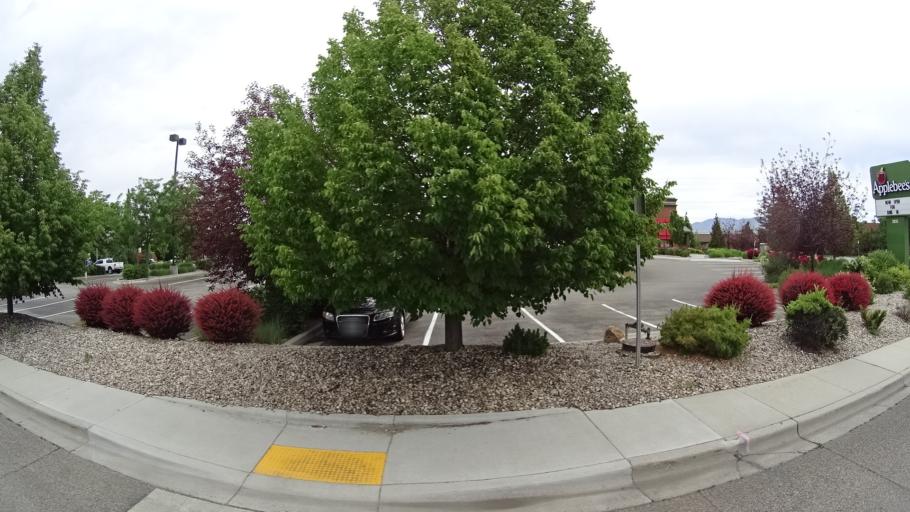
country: US
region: Idaho
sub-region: Ada County
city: Boise
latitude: 43.5735
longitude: -116.2163
